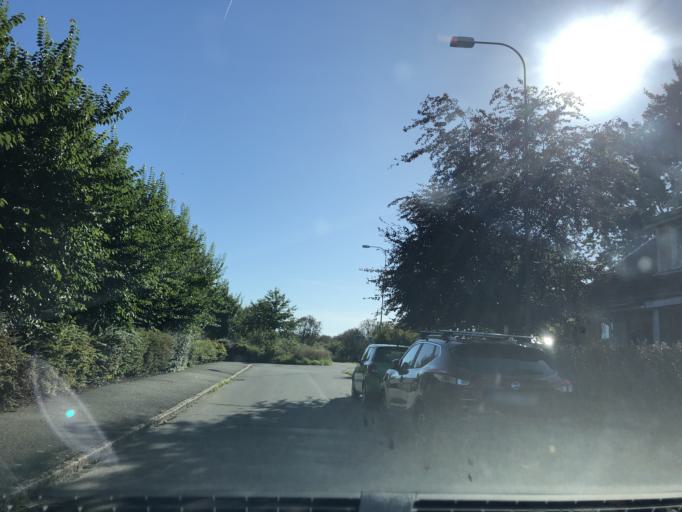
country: SE
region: Vaestra Goetaland
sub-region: Goteborg
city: Majorna
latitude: 57.6603
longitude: 11.8797
